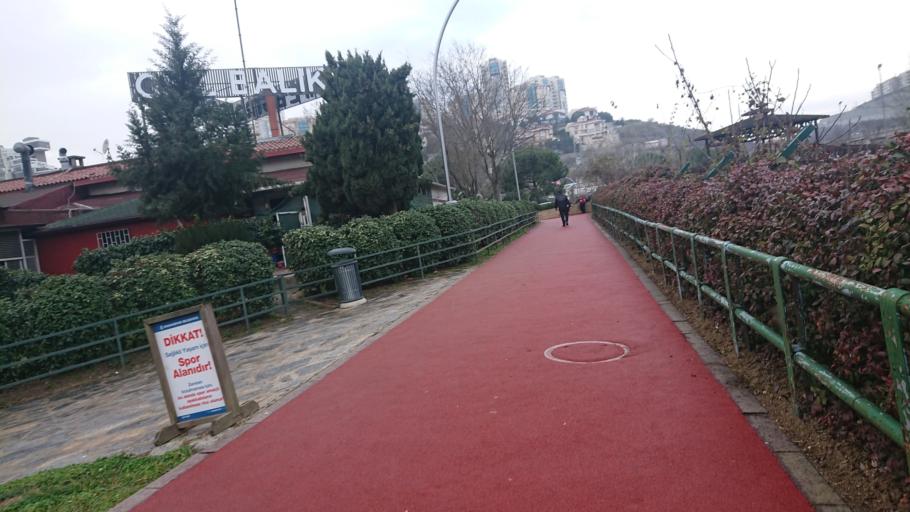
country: TR
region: Istanbul
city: Esenyurt
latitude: 41.0705
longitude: 28.6922
